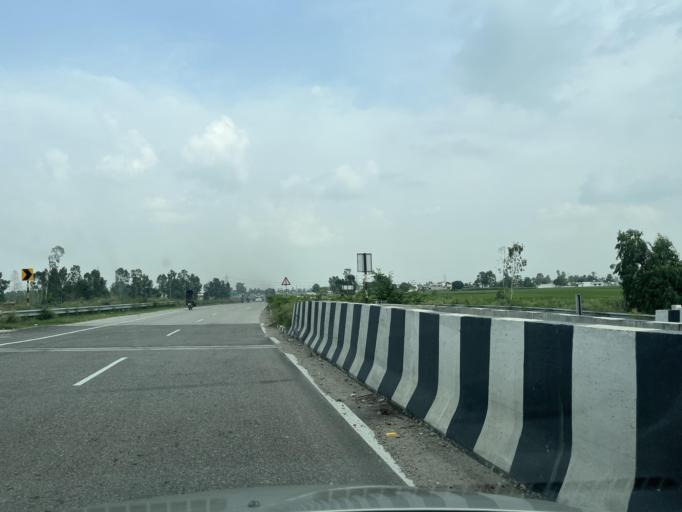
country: IN
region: Uttarakhand
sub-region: Udham Singh Nagar
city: Bazpur
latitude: 29.1508
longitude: 79.0707
